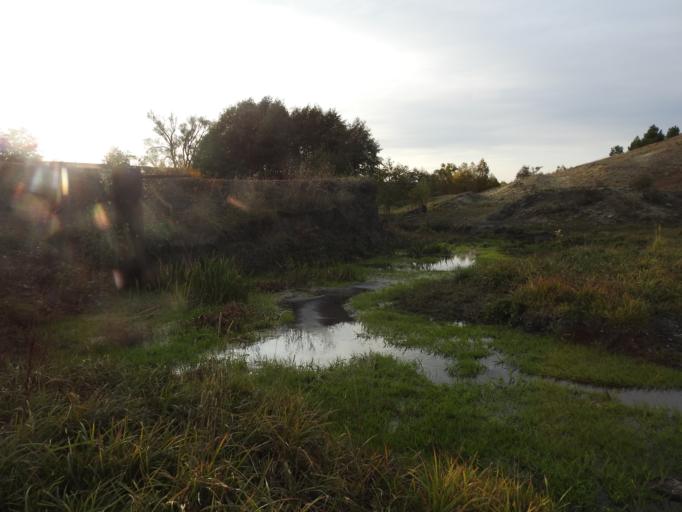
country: RU
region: Saratov
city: Baltay
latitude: 52.5630
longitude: 46.6589
